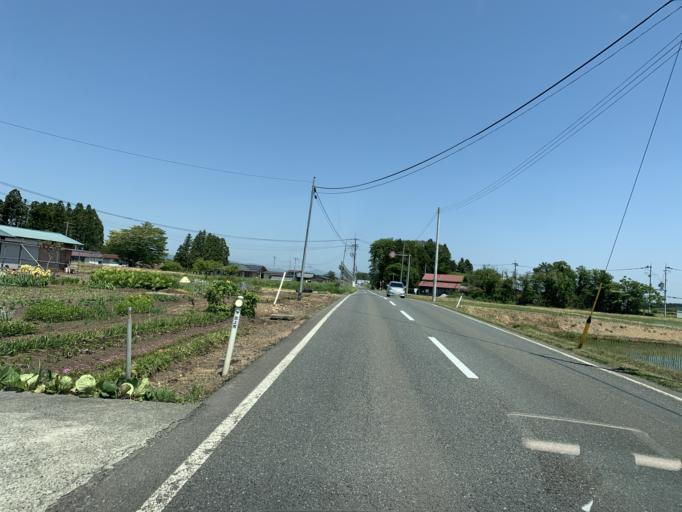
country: JP
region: Iwate
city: Kitakami
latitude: 39.2533
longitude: 141.0653
